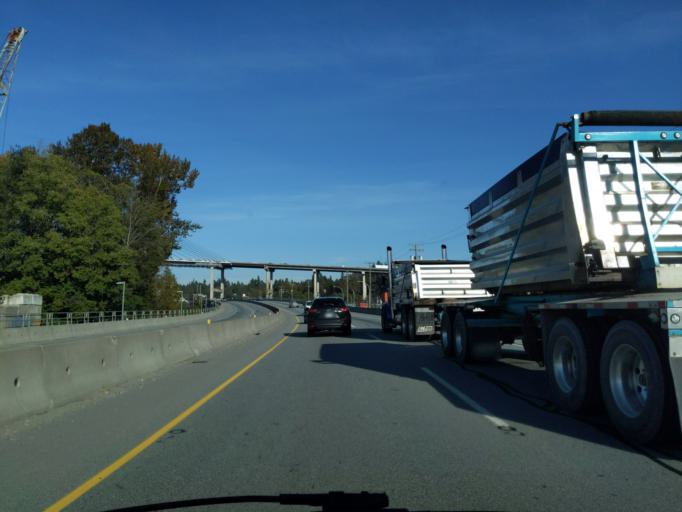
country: CA
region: British Columbia
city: Delta
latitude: 49.1535
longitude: -122.9473
